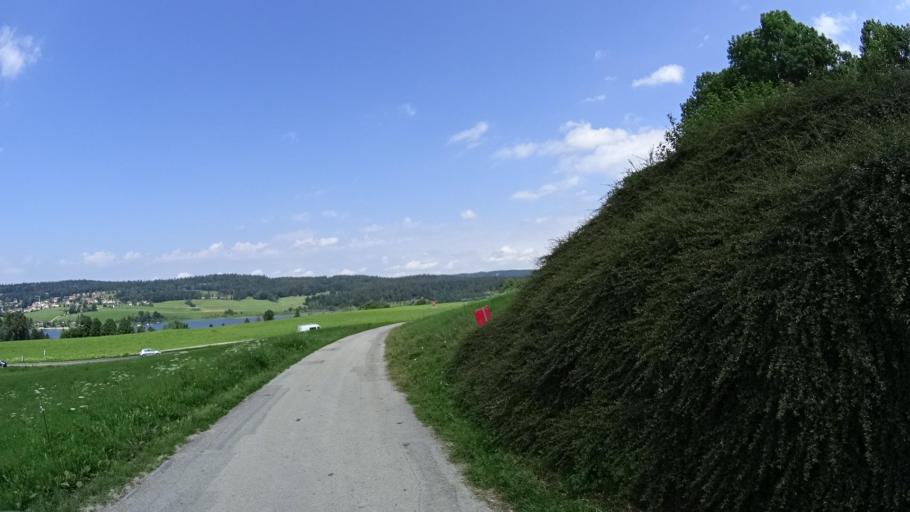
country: FR
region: Franche-Comte
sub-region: Departement du Doubs
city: Les Fourgs
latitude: 46.8220
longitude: 6.3323
